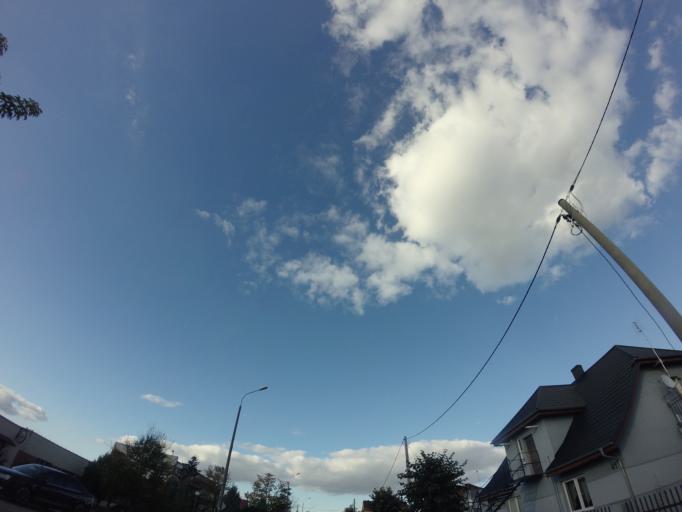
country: PL
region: Greater Poland Voivodeship
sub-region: Powiat nowotomyski
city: Nowy Tomysl
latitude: 52.3011
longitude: 16.1276
